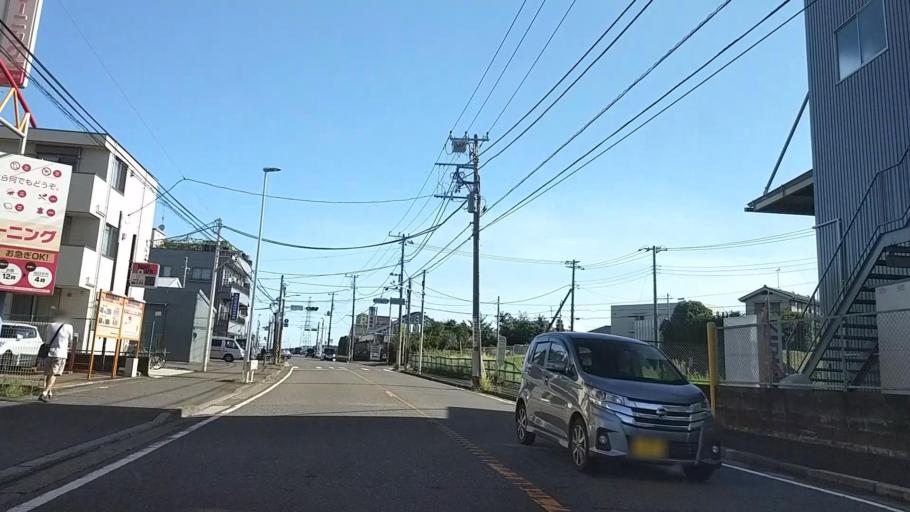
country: JP
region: Kanagawa
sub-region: Kawasaki-shi
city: Kawasaki
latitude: 35.5363
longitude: 139.6541
